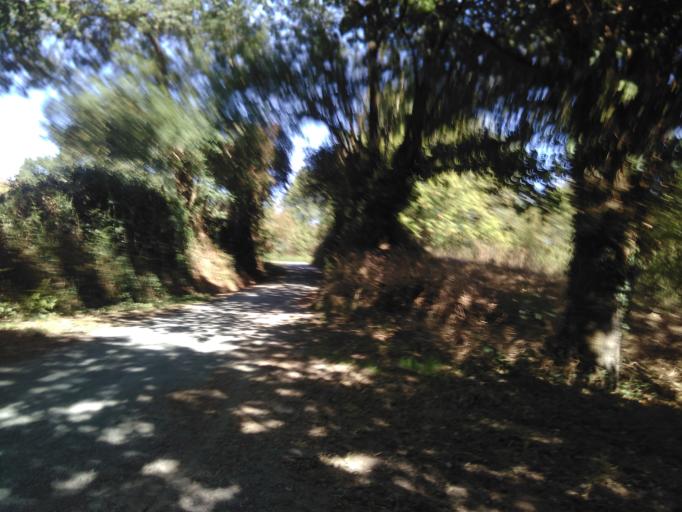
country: FR
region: Pays de la Loire
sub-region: Departement de la Vendee
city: La Chaize-le-Vicomte
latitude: 46.6681
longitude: -1.2974
